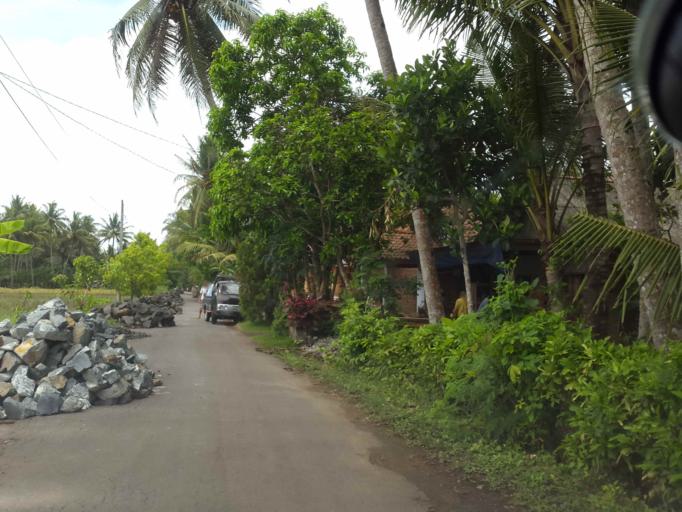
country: ID
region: Central Java
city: Kutoarjo
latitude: -7.7523
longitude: 109.8406
